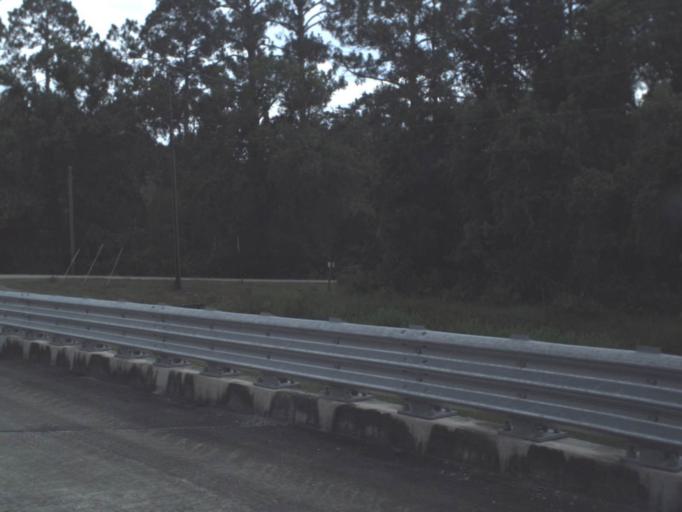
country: US
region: Florida
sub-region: Levy County
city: Chiefland
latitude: 29.3317
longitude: -82.7713
